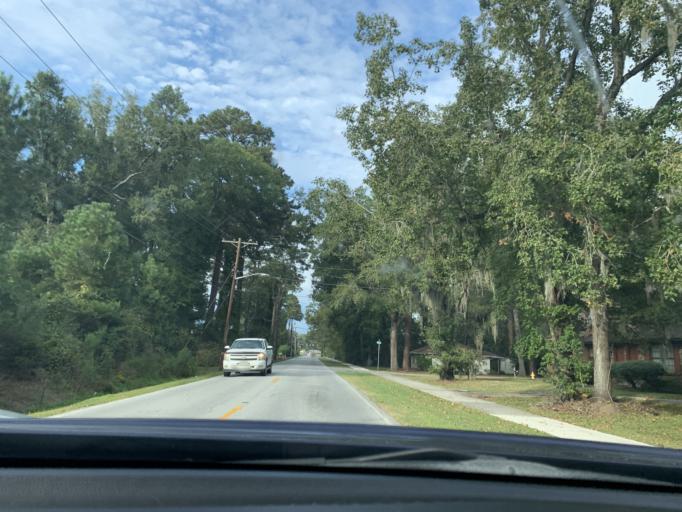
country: US
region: Georgia
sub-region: Chatham County
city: Pooler
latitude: 32.1117
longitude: -81.2503
